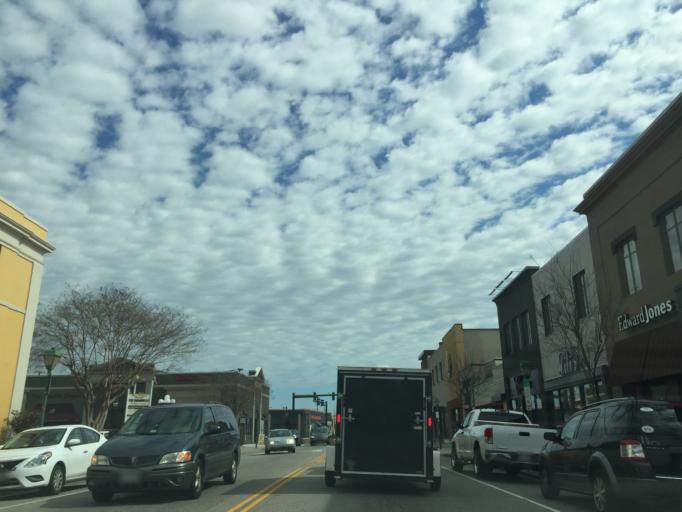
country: US
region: Virginia
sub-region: City of Norfolk
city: Norfolk
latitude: 36.8686
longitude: -76.2895
